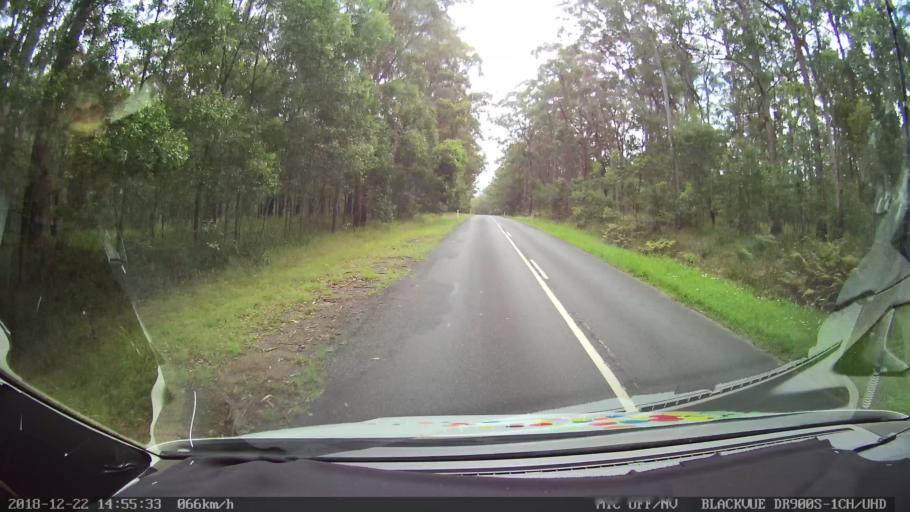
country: AU
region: New South Wales
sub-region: Bellingen
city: Dorrigo
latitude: -30.2302
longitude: 152.5202
